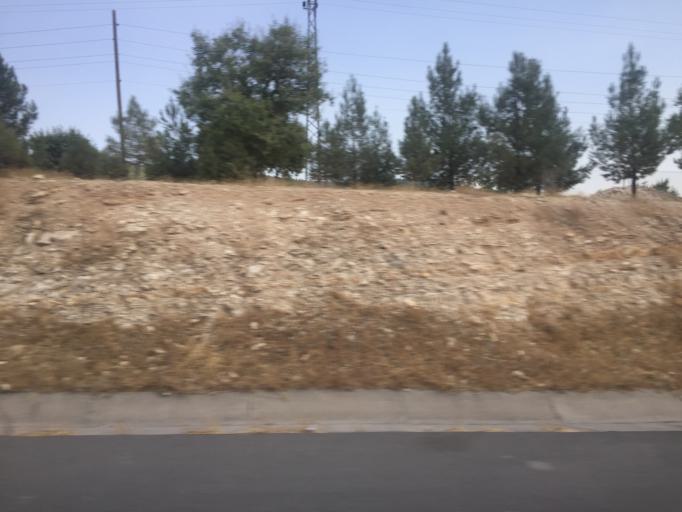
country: TR
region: Sanliurfa
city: Akziyaret
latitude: 37.2657
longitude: 38.7993
